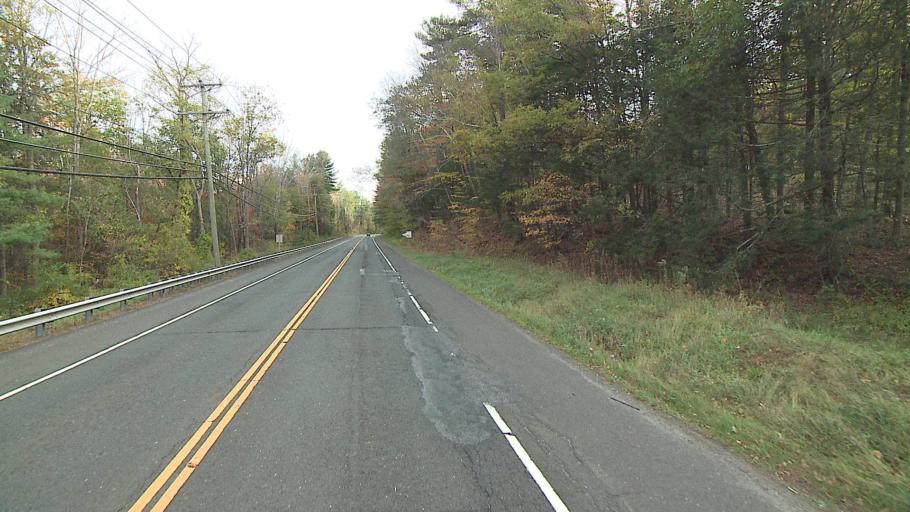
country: US
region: Connecticut
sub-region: Litchfield County
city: New Hartford Center
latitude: 41.8951
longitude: -72.9880
